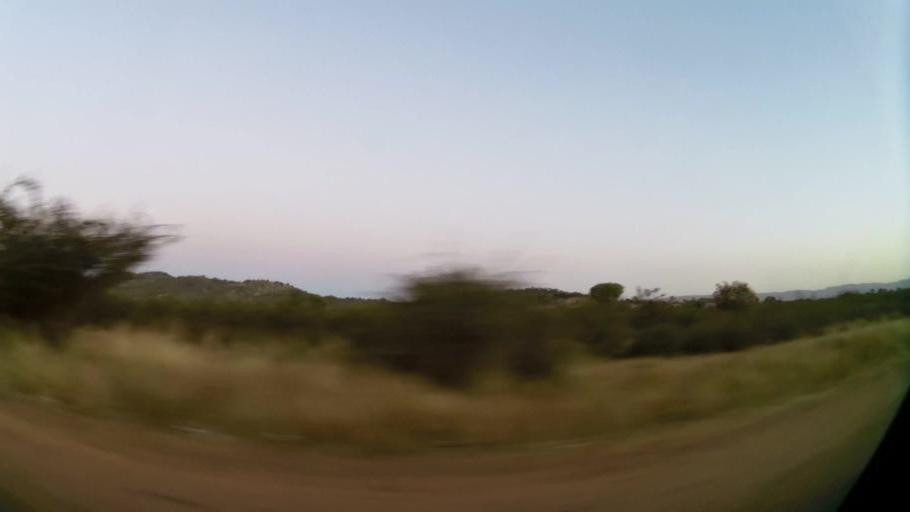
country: ZA
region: North-West
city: Ga-Rankuwa
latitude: -25.6298
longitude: 27.9604
